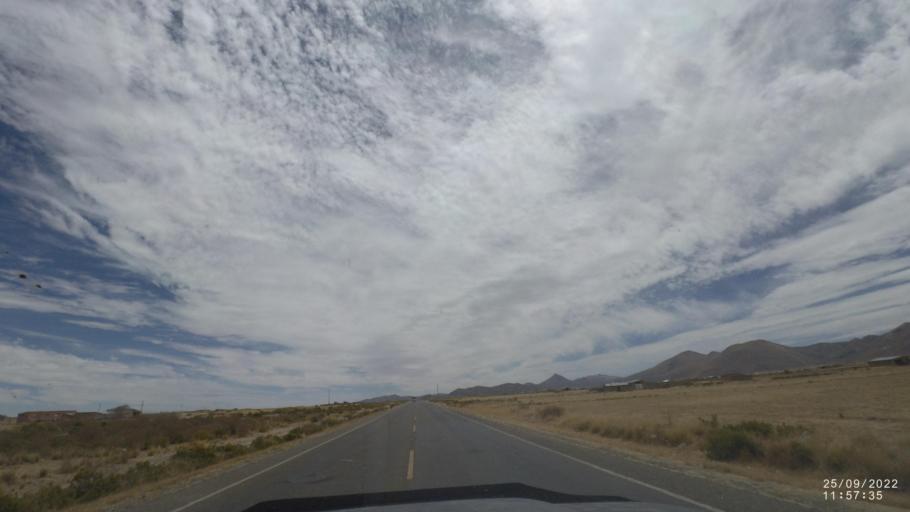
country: BO
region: Oruro
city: Challapata
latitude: -18.8201
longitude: -66.8288
